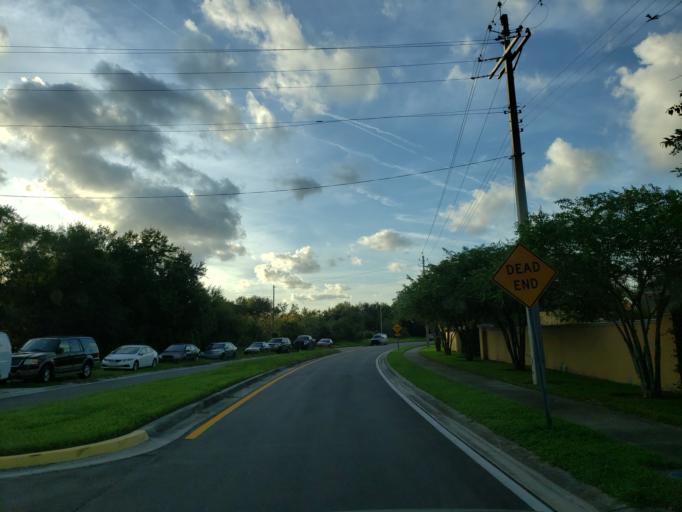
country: US
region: Florida
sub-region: Hillsborough County
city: Brandon
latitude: 27.9029
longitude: -82.2975
